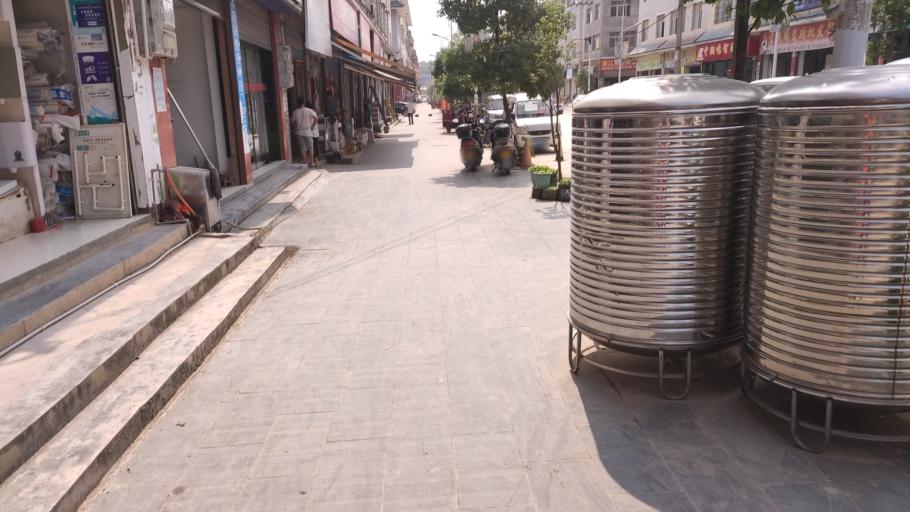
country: CN
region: Guizhou Sheng
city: Zhongchao
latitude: 26.1377
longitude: 109.2179
